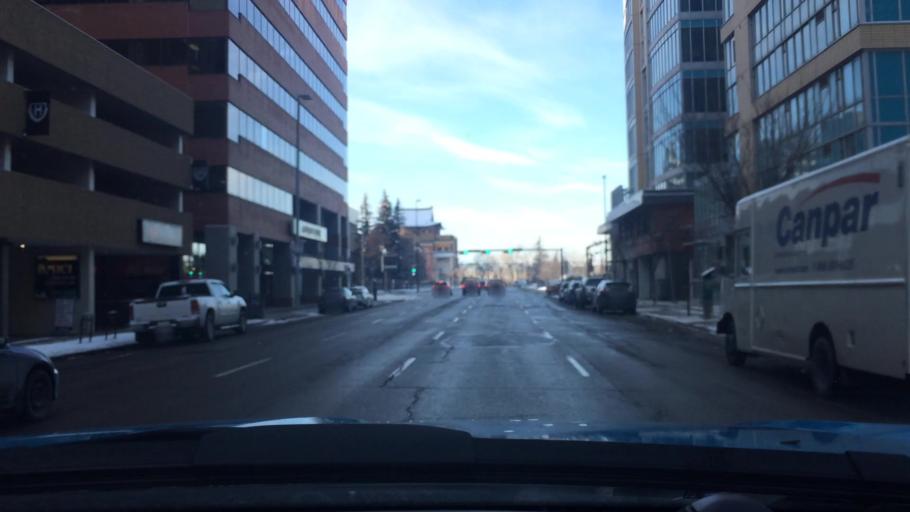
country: CA
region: Alberta
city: Calgary
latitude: 51.0498
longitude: -114.0794
